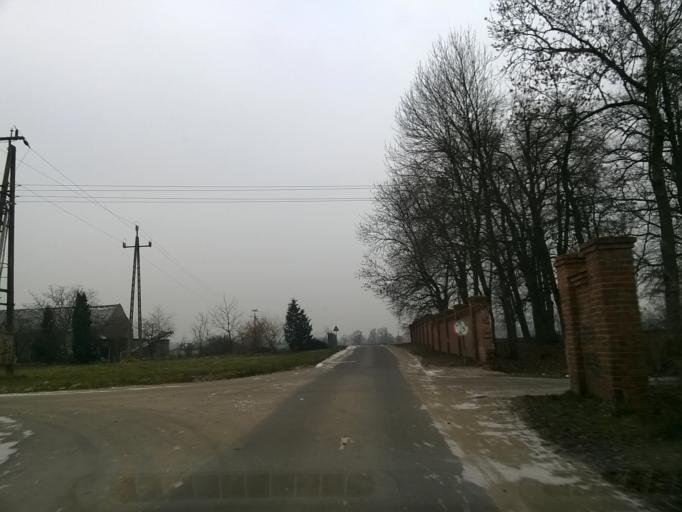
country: PL
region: Kujawsko-Pomorskie
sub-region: Powiat nakielski
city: Kcynia
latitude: 53.0087
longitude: 17.5008
